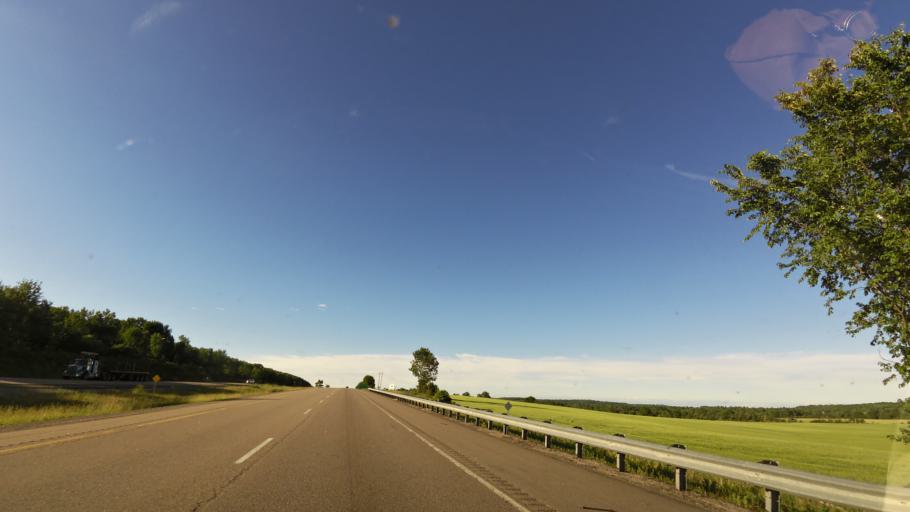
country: CA
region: Ontario
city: Orillia
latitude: 44.6485
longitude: -79.6494
